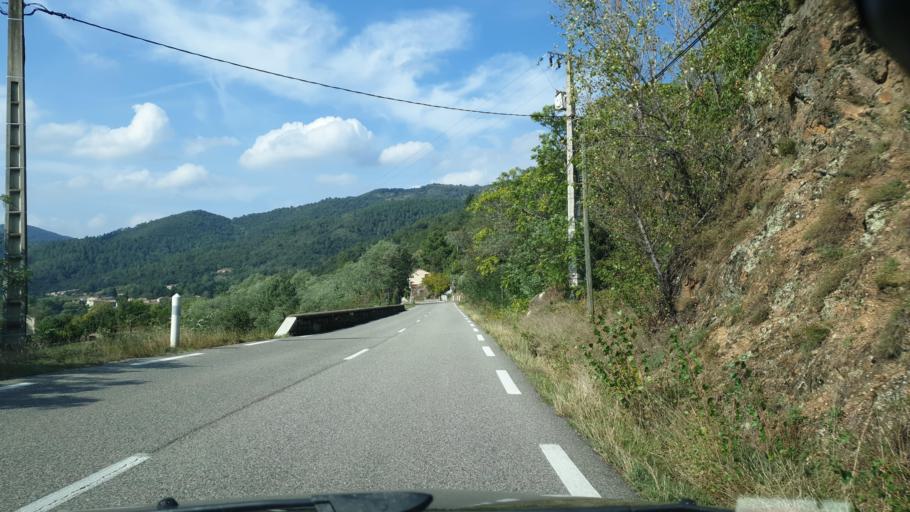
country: FR
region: Rhone-Alpes
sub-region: Departement de l'Ardeche
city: Saint-Laurent-du-Pape
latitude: 44.8278
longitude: 4.6907
